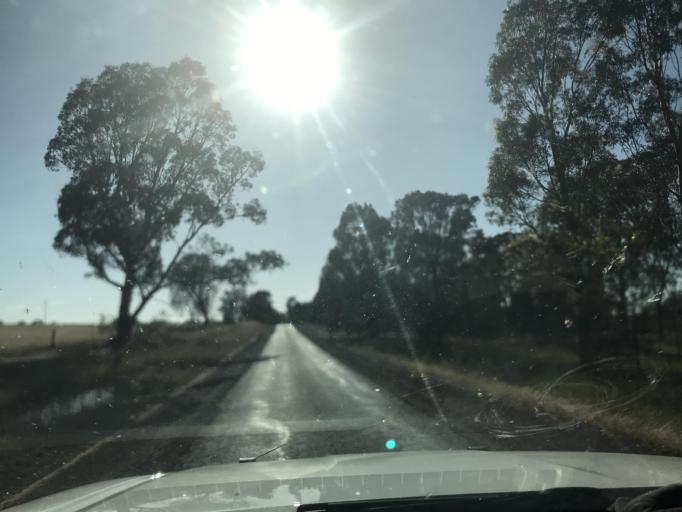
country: AU
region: Victoria
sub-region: Horsham
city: Horsham
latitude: -37.0049
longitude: 141.6185
